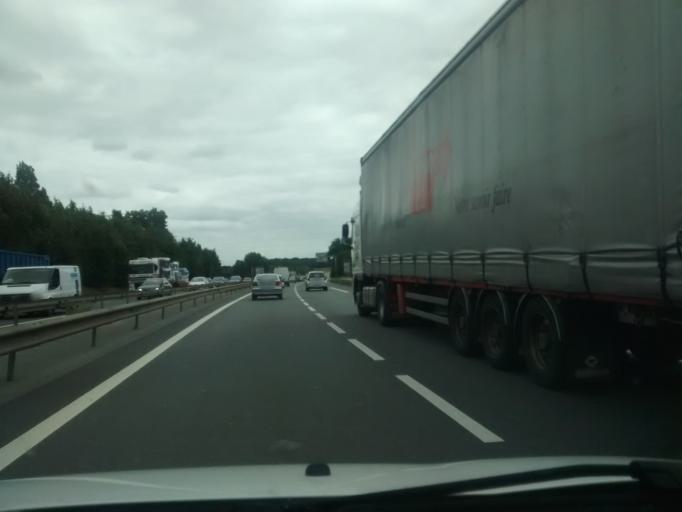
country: FR
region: Brittany
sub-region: Departement d'Ille-et-Vilaine
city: Saint-Jacques-de-la-Lande
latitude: 48.0861
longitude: -1.7001
